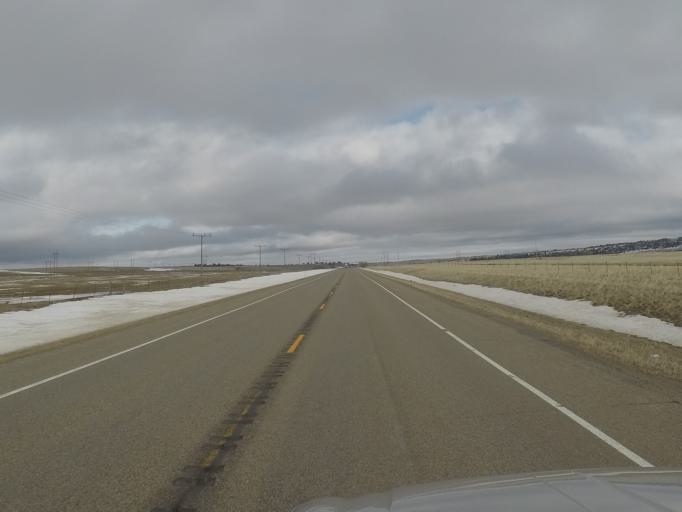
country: US
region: Montana
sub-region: Golden Valley County
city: Ryegate
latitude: 46.3281
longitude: -109.4679
